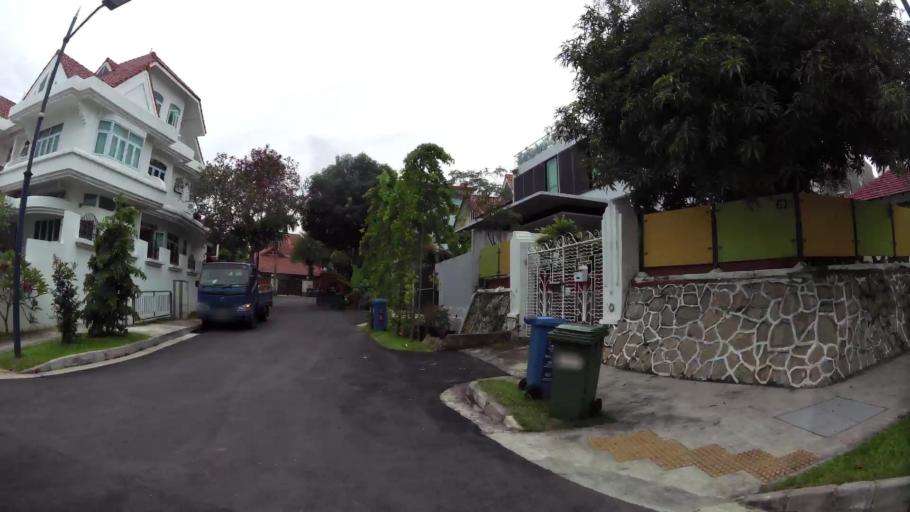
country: SG
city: Singapore
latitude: 1.3586
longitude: 103.8649
